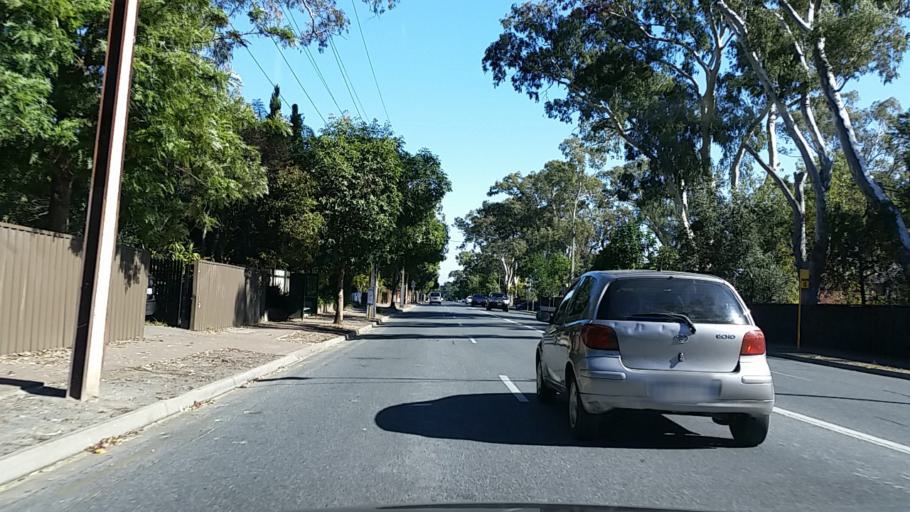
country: AU
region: South Australia
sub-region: Burnside
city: Kensington Gardens
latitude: -34.9256
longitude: 138.6673
